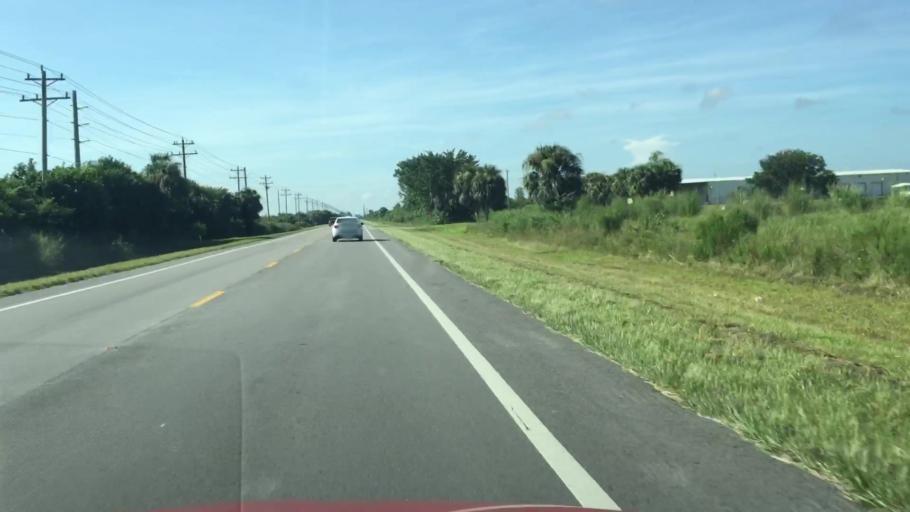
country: US
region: Florida
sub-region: Collier County
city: Immokalee
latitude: 26.3869
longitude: -81.4171
